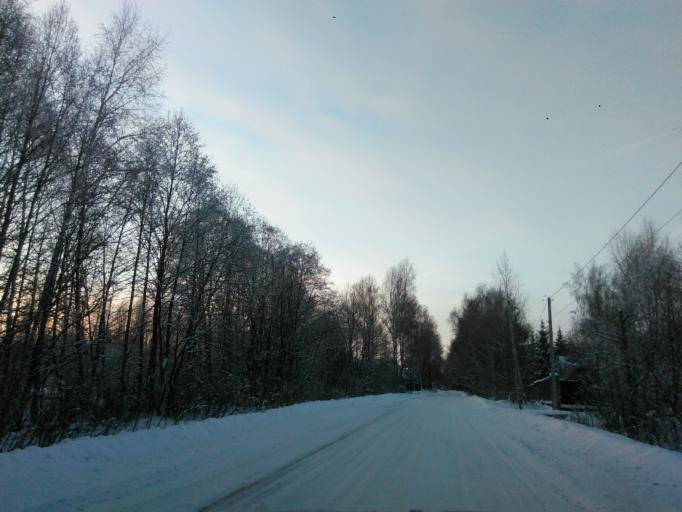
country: RU
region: Tverskaya
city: Zavidovo
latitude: 56.6426
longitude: 36.6297
